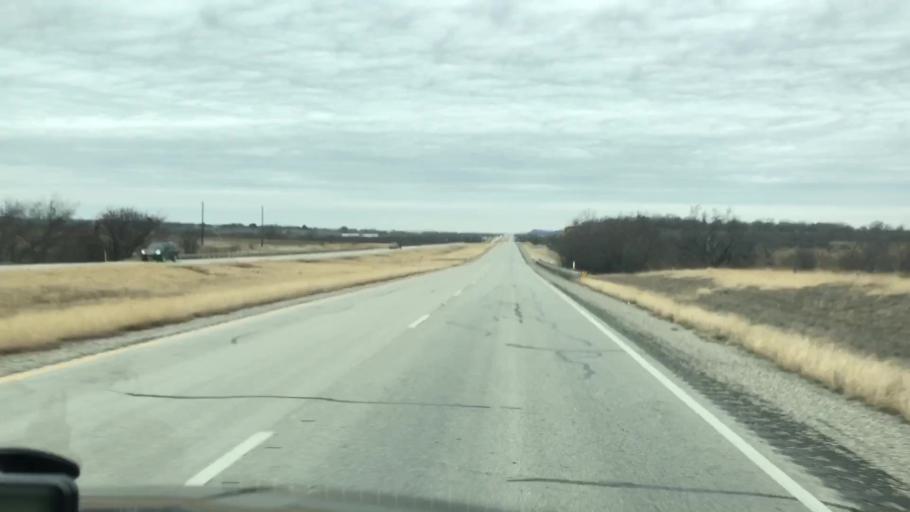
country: US
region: Texas
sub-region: Jack County
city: Jacksboro
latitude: 33.2364
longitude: -98.2073
